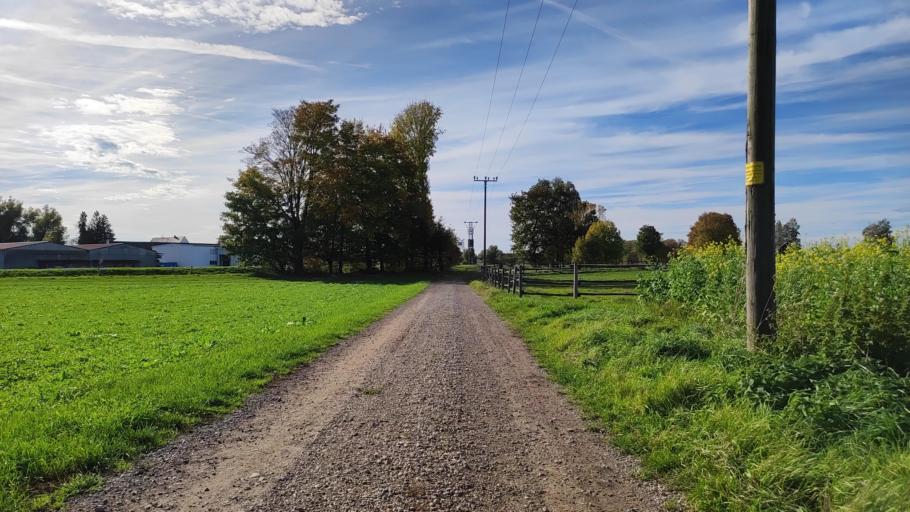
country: DE
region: Bavaria
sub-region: Swabia
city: Pfaffenhausen
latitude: 48.1249
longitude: 10.4593
